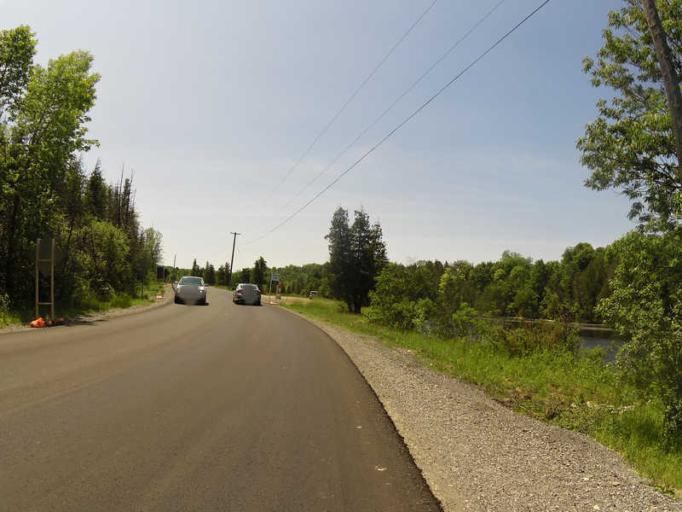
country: CA
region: Ontario
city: Peterborough
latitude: 44.3712
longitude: -78.2897
